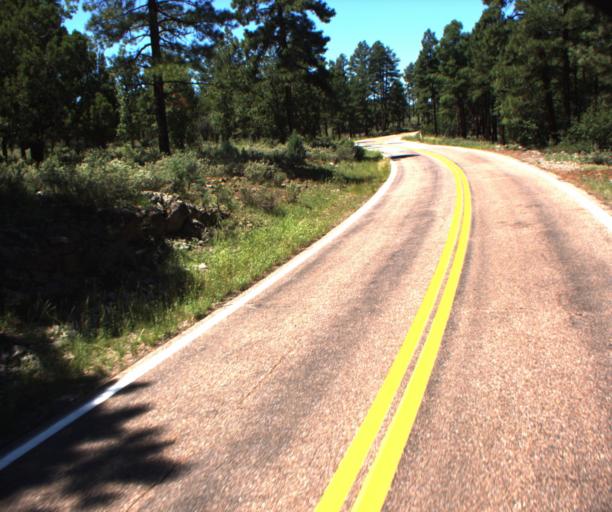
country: US
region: Arizona
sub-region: Greenlee County
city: Morenci
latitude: 33.4872
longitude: -109.3444
